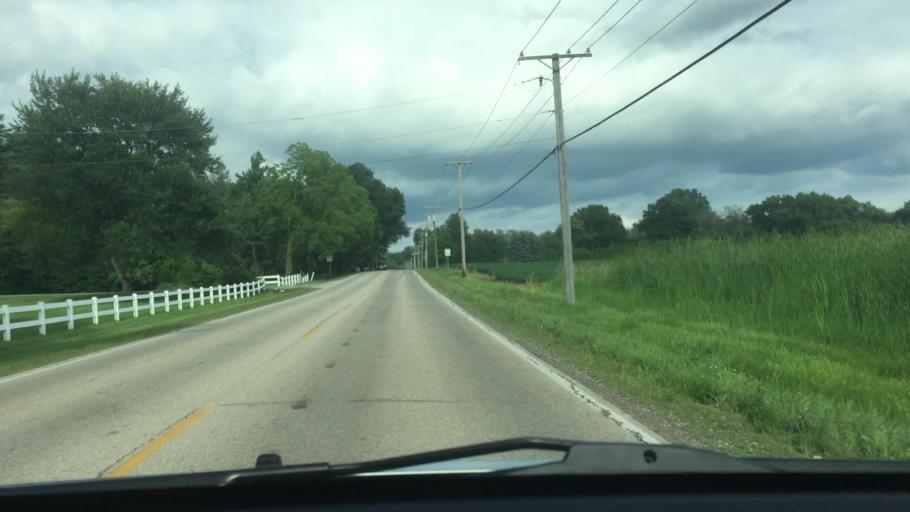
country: US
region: Illinois
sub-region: McHenry County
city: Lakewood
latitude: 42.2681
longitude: -88.3532
